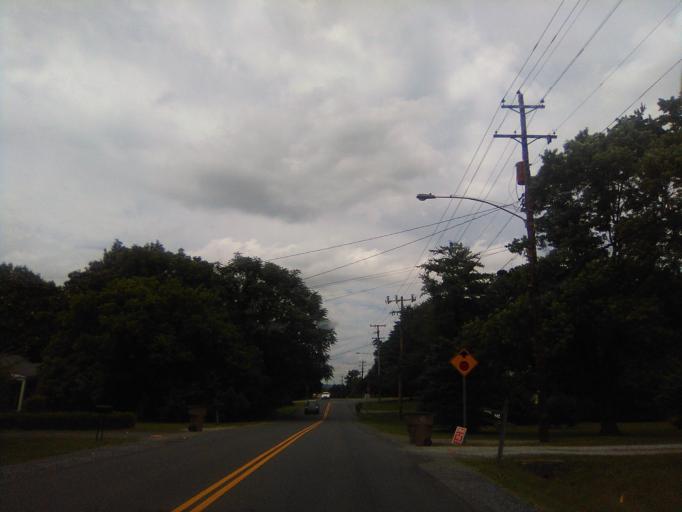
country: US
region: Tennessee
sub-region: Davidson County
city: Belle Meade
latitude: 36.1328
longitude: -86.8837
